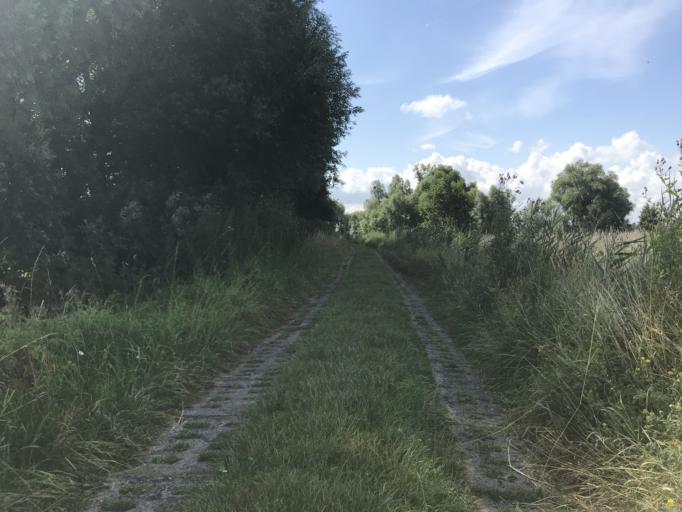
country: PL
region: Pomeranian Voivodeship
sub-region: Gdansk
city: Gdansk
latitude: 54.3213
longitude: 18.6722
